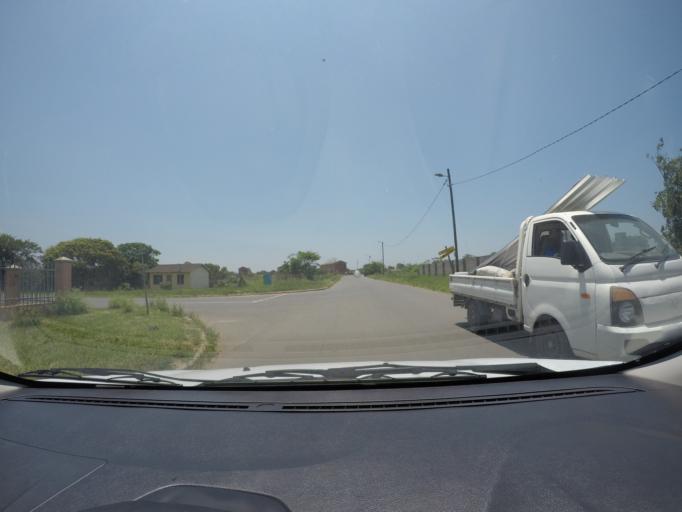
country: ZA
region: KwaZulu-Natal
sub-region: uThungulu District Municipality
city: eSikhawini
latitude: -28.8762
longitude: 31.8997
